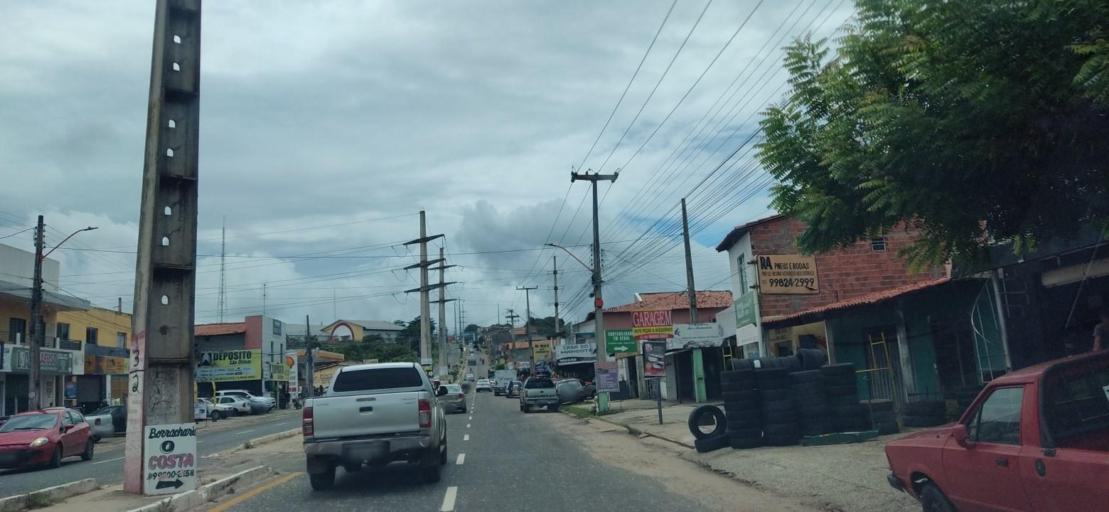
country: BR
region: Piaui
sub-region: Teresina
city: Teresina
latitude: -5.0590
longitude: -42.7526
